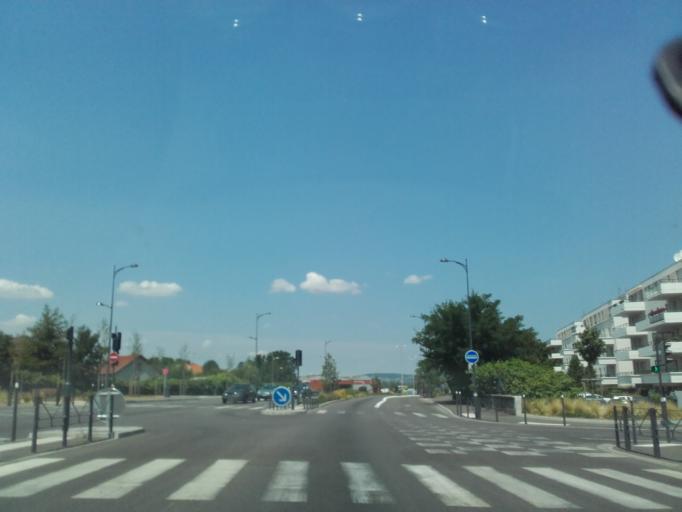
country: FR
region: Rhone-Alpes
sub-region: Departement de l'Isere
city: Bourgoin-Jallieu
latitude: 45.5907
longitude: 5.2721
